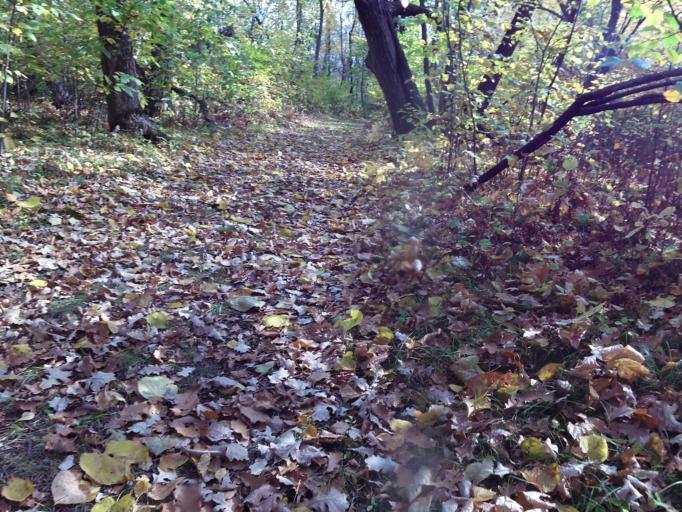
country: US
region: North Dakota
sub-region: Pembina County
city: Cavalier
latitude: 48.7784
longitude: -97.7386
